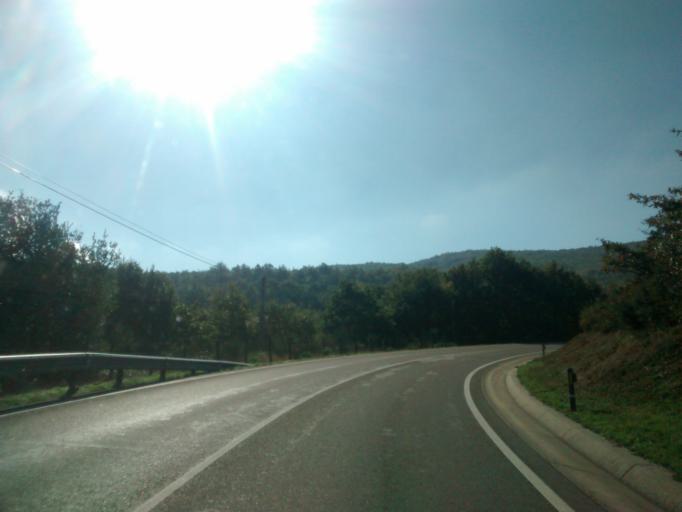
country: ES
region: Cantabria
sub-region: Provincia de Cantabria
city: Reinosa
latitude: 42.9744
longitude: -4.0963
